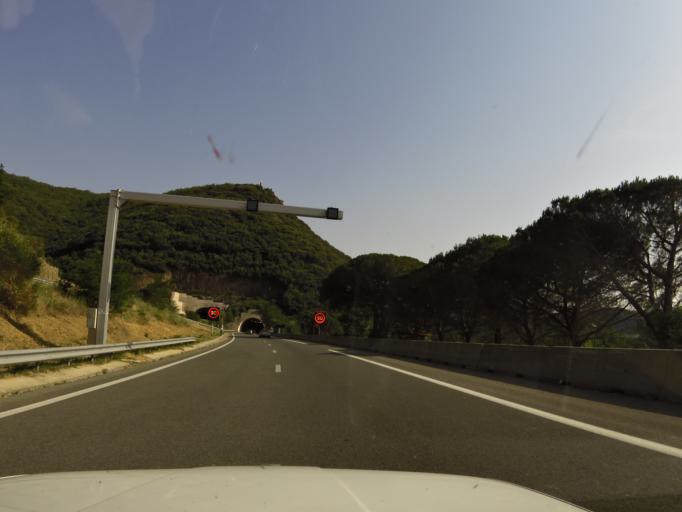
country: FR
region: Languedoc-Roussillon
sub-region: Departement de l'Herault
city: Lodeve
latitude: 43.7316
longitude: 3.3267
